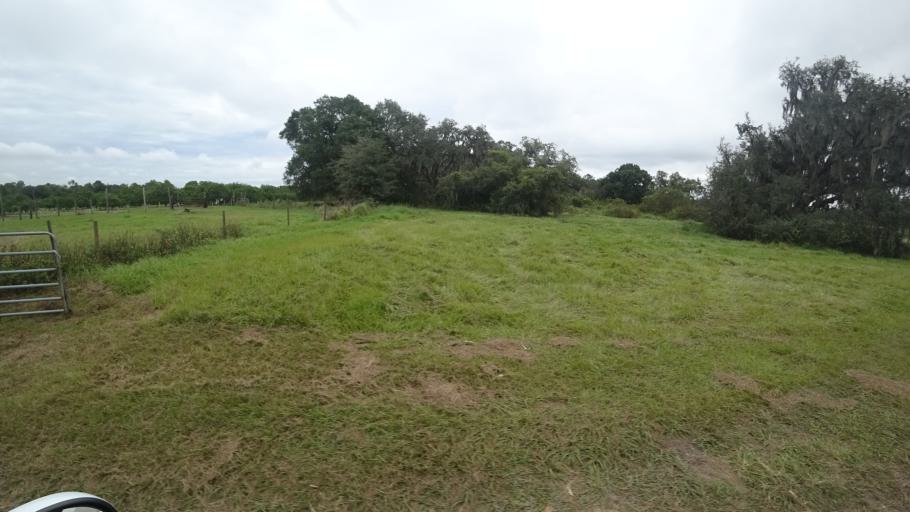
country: US
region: Florida
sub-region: Hillsborough County
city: Wimauma
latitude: 27.5706
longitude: -82.1374
